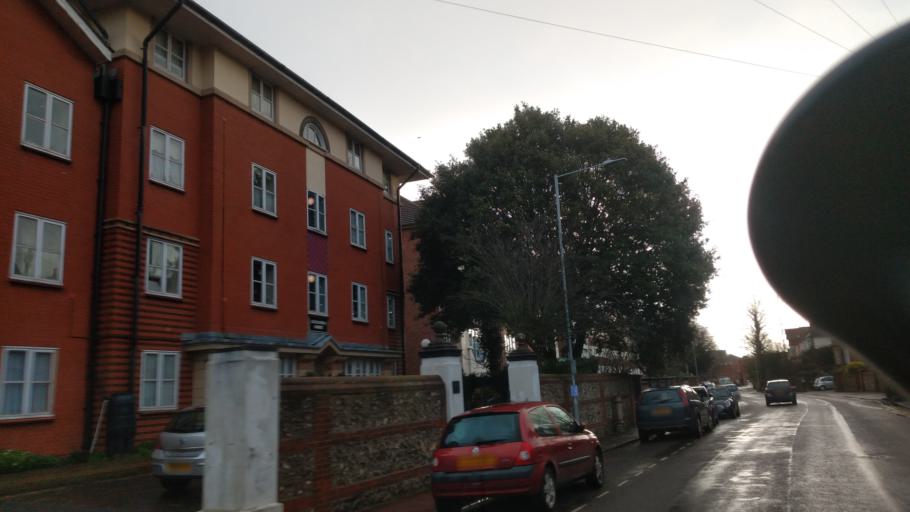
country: GB
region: England
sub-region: East Sussex
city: Eastbourne
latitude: 50.7705
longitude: 0.2758
